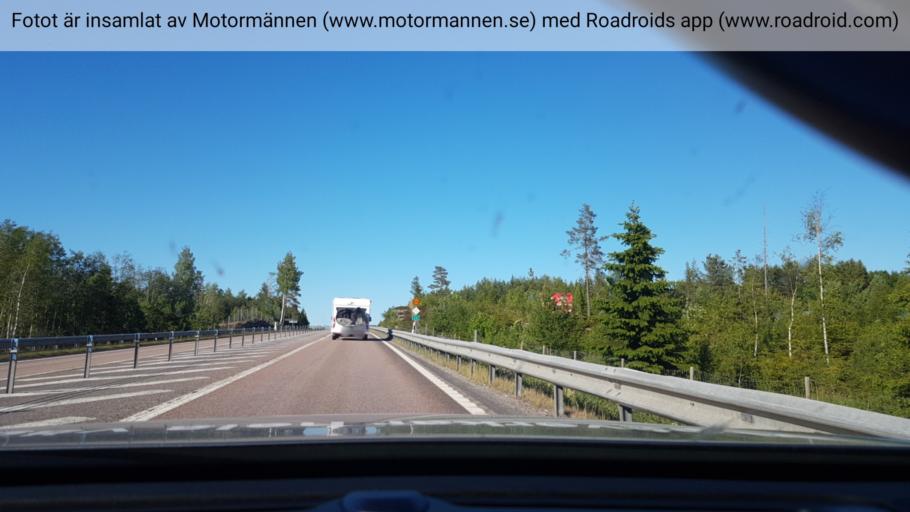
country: SE
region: Vaesternorrland
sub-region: Haernoesands Kommun
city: Haernoesand
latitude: 62.6002
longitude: 17.8114
